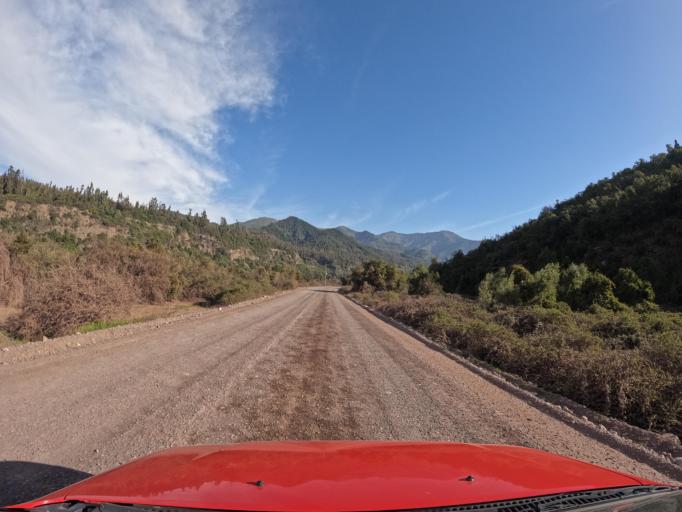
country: CL
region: O'Higgins
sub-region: Provincia de Colchagua
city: Chimbarongo
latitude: -34.9992
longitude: -70.8261
